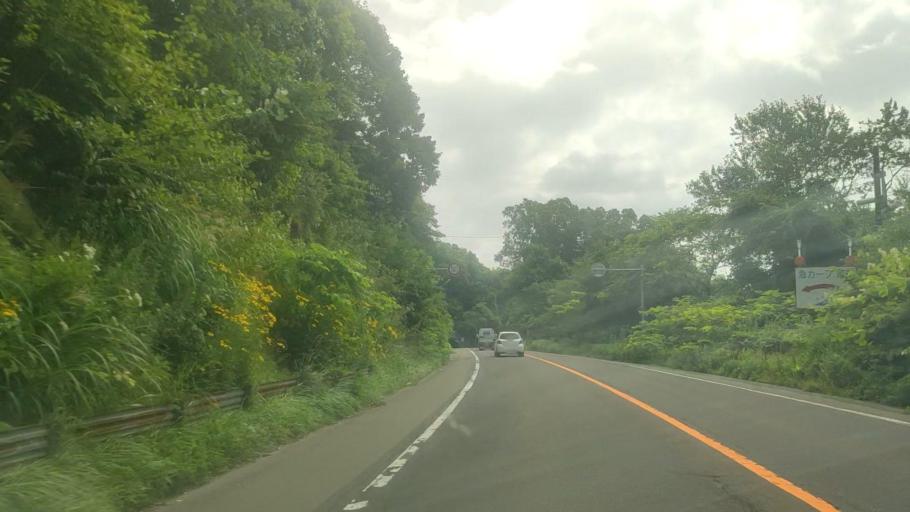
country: JP
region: Hokkaido
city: Niseko Town
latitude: 42.5912
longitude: 140.6754
